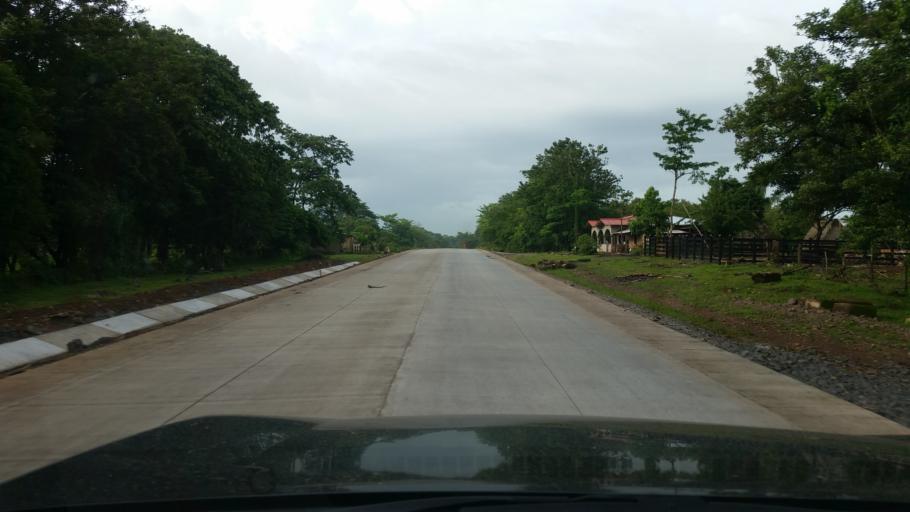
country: NI
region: Matagalpa
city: Rio Blanco
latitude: 13.1123
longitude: -85.0638
